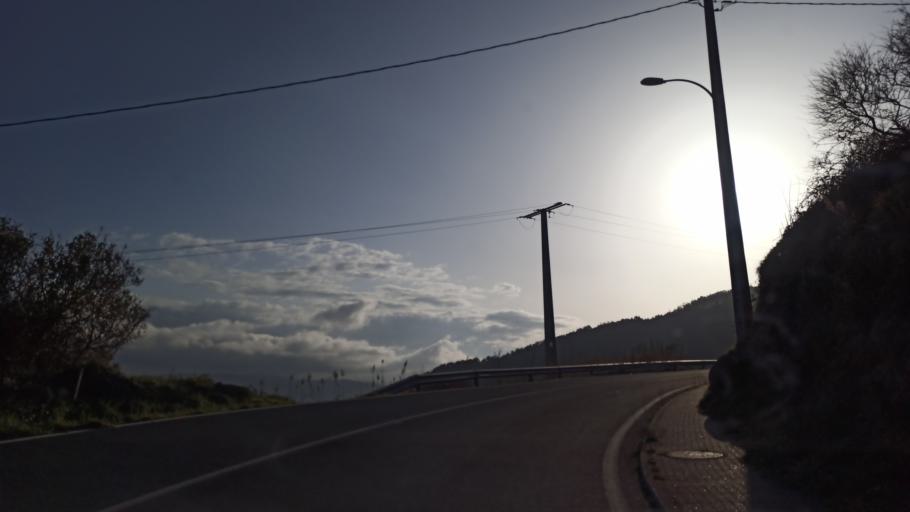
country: ES
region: Galicia
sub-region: Provincia de Lugo
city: Viveiro
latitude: 43.7730
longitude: -7.6717
